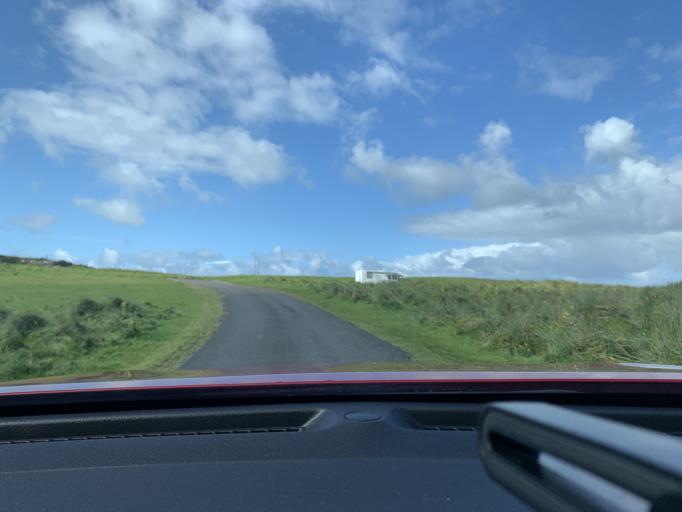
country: IE
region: Connaught
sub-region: Sligo
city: Strandhill
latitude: 54.3979
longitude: -8.5660
